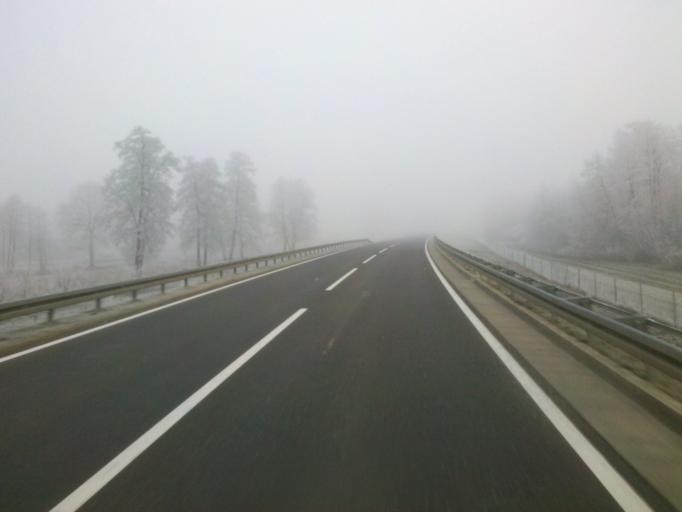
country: HR
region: Varazdinska
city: Jalkovec
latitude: 46.2756
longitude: 16.3039
